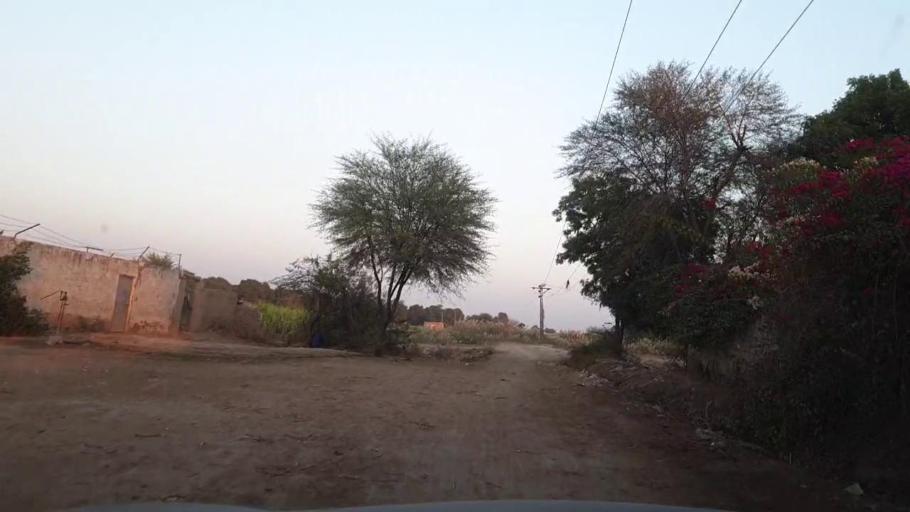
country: PK
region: Sindh
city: Tando Allahyar
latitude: 25.5058
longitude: 68.7492
